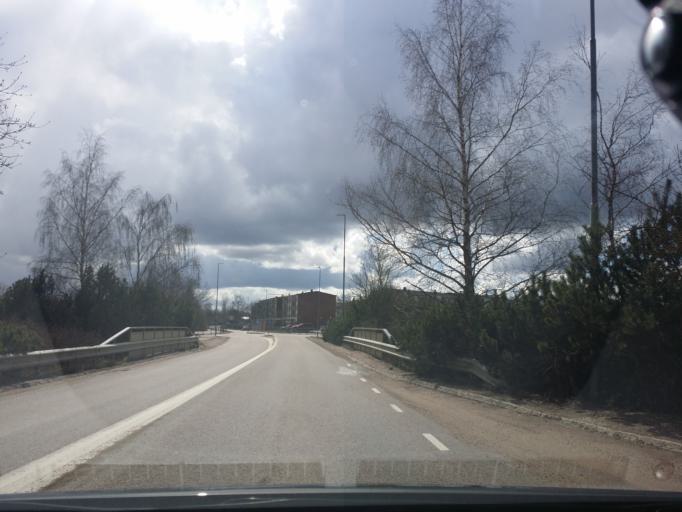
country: SE
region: Vaestmanland
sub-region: Sala Kommun
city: Sala
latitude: 59.9272
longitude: 16.5904
